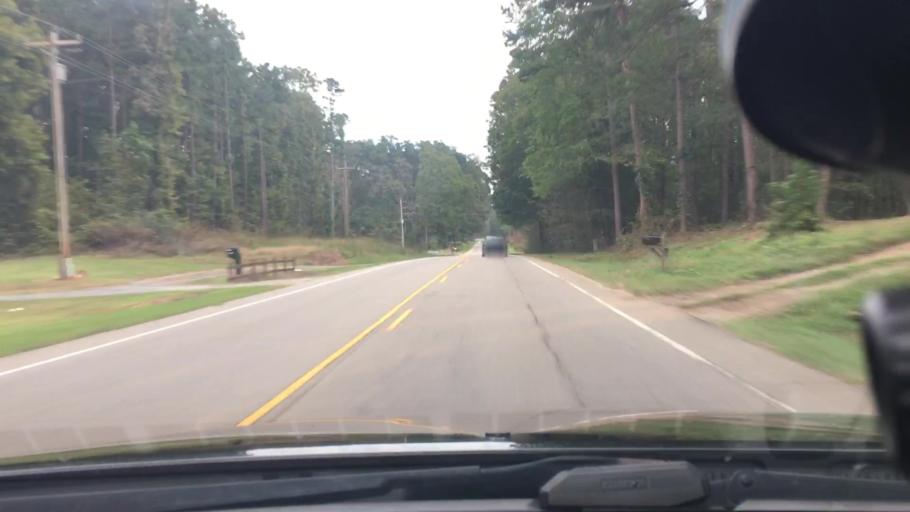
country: US
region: North Carolina
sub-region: Moore County
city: Robbins
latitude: 35.3943
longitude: -79.5264
